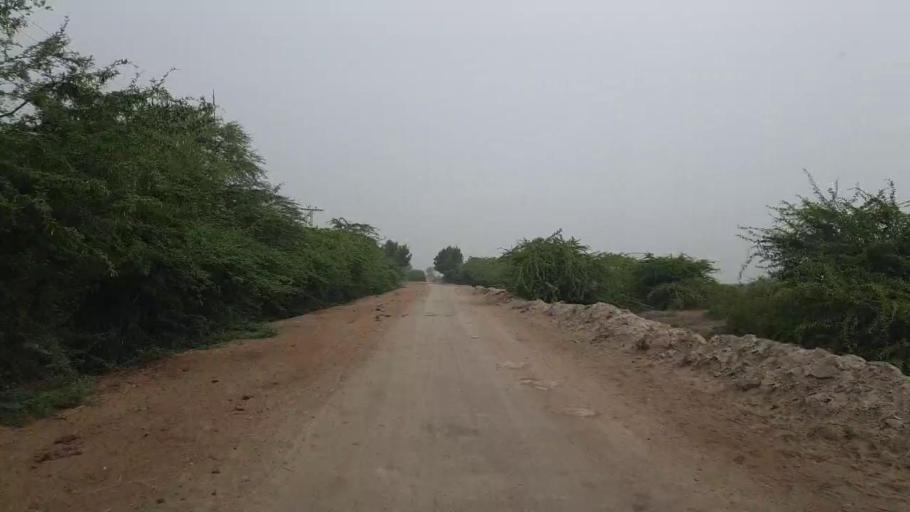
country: PK
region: Sindh
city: Badin
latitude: 24.5862
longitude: 68.6666
